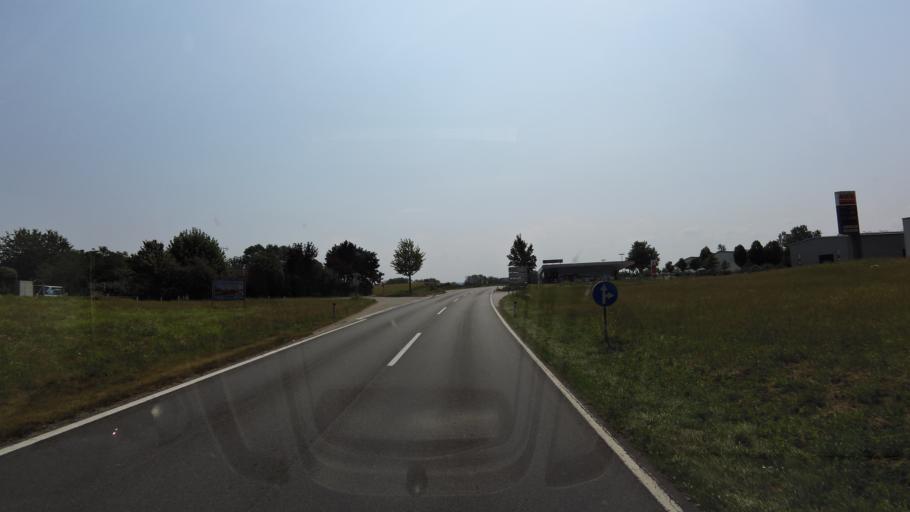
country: DE
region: Bavaria
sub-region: Lower Bavaria
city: Bad Fussing
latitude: 48.3143
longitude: 13.3253
